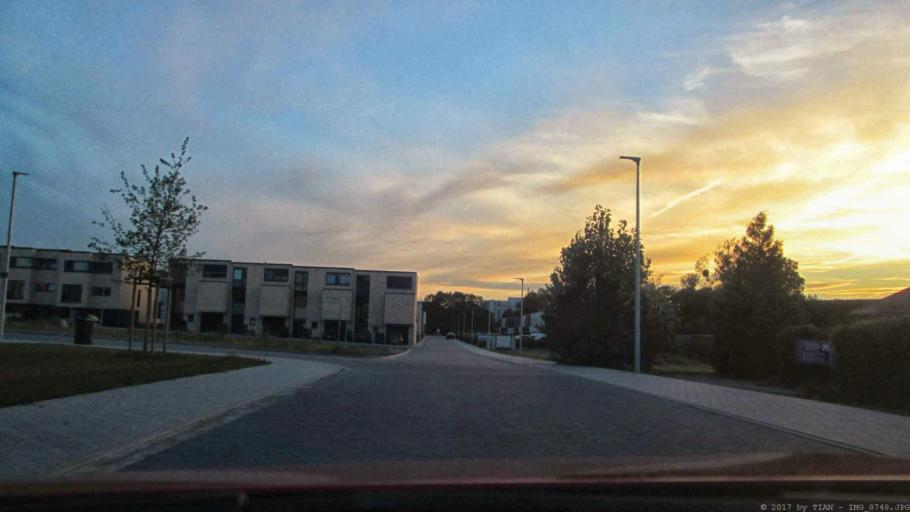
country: DE
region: Lower Saxony
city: Wolfsburg
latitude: 52.4059
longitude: 10.7488
